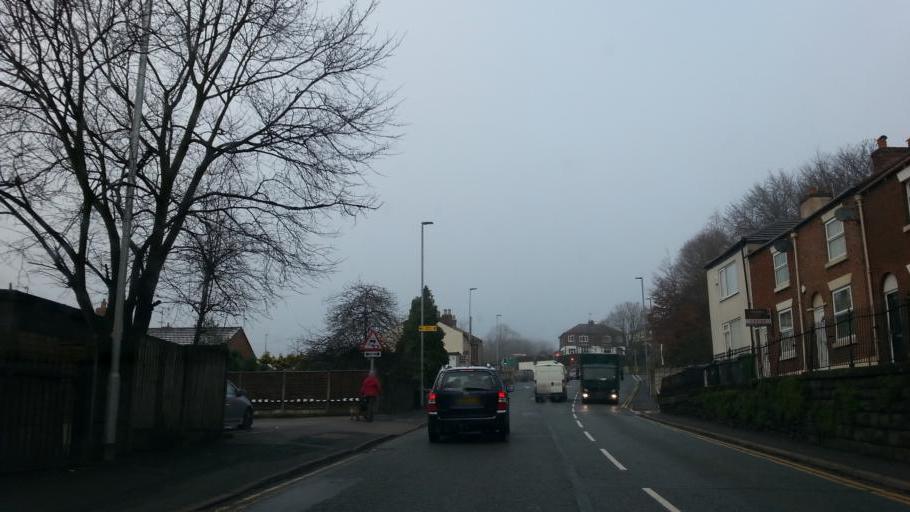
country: GB
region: England
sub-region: Cheshire East
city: Congleton
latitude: 53.1677
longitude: -2.2142
